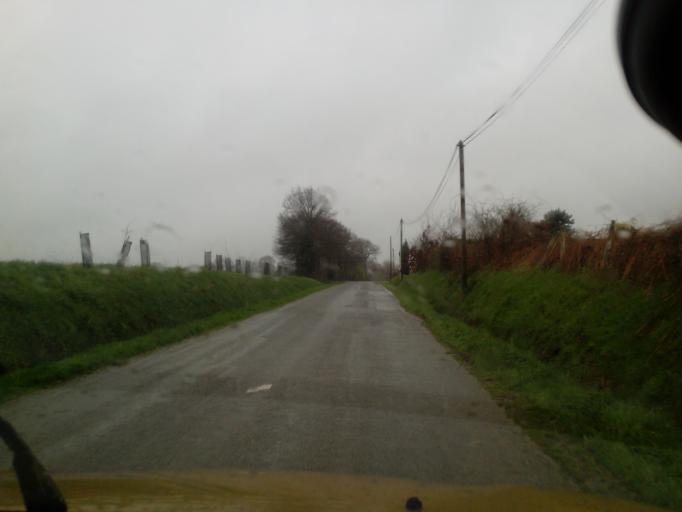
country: FR
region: Brittany
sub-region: Departement d'Ille-et-Vilaine
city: Chevaigne
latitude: 48.2173
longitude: -1.6603
